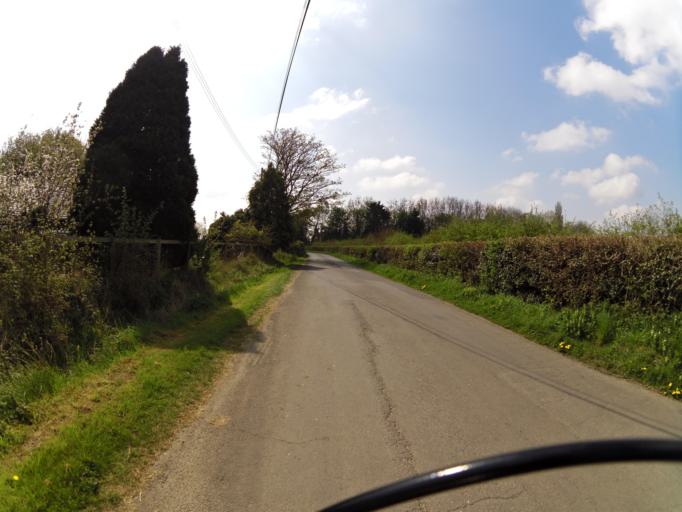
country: GB
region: England
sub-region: Suffolk
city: Bramford
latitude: 52.0820
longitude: 1.0410
